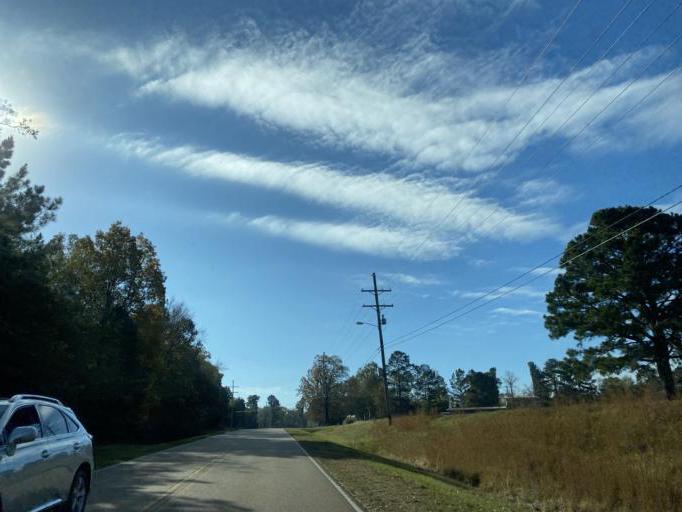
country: US
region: Mississippi
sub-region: Madison County
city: Ridgeland
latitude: 32.4726
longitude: -90.1792
